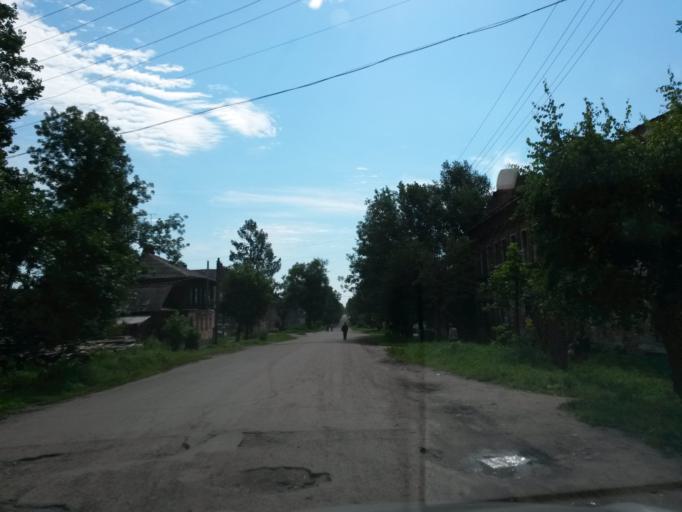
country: RU
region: Jaroslavl
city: Tutayev
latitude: 57.8833
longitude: 39.5440
